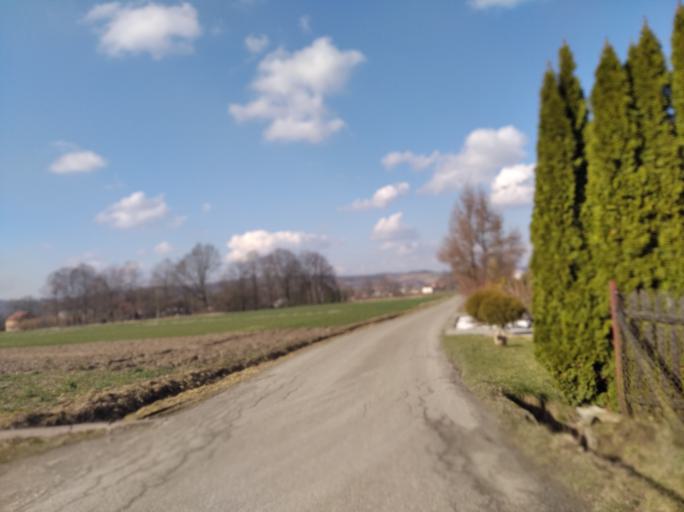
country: PL
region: Subcarpathian Voivodeship
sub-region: Powiat strzyzowski
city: Wysoka Strzyzowska
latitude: 49.8562
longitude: 21.7091
